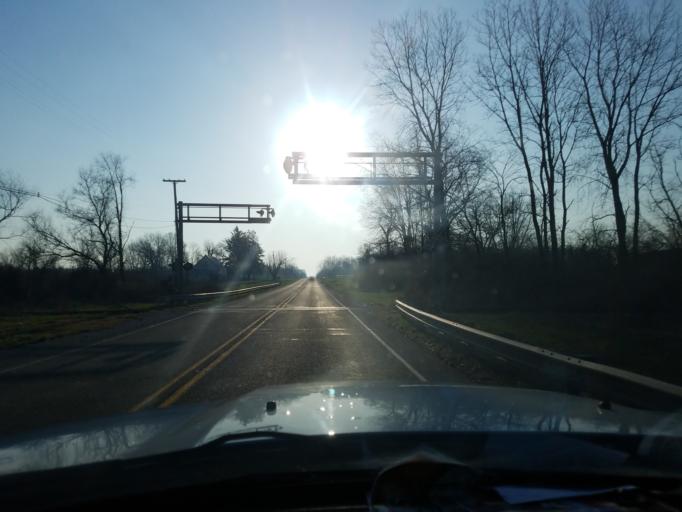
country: US
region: Indiana
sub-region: Vigo County
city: Seelyville
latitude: 39.3903
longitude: -87.2707
